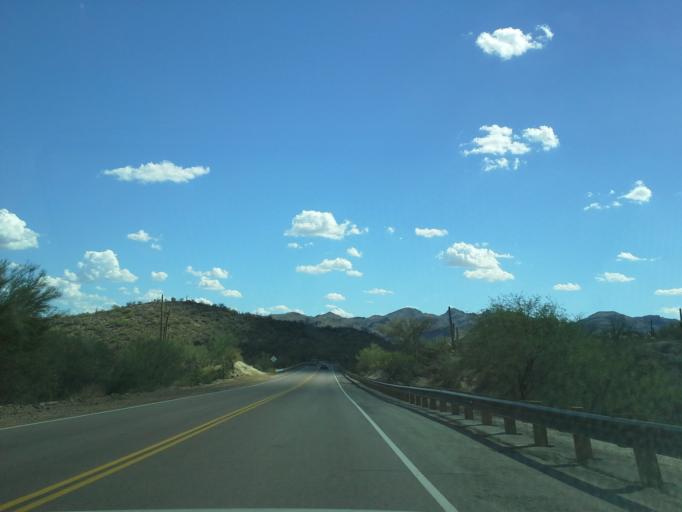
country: US
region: Arizona
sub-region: Pinal County
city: Apache Junction
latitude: 33.5859
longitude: -111.5415
